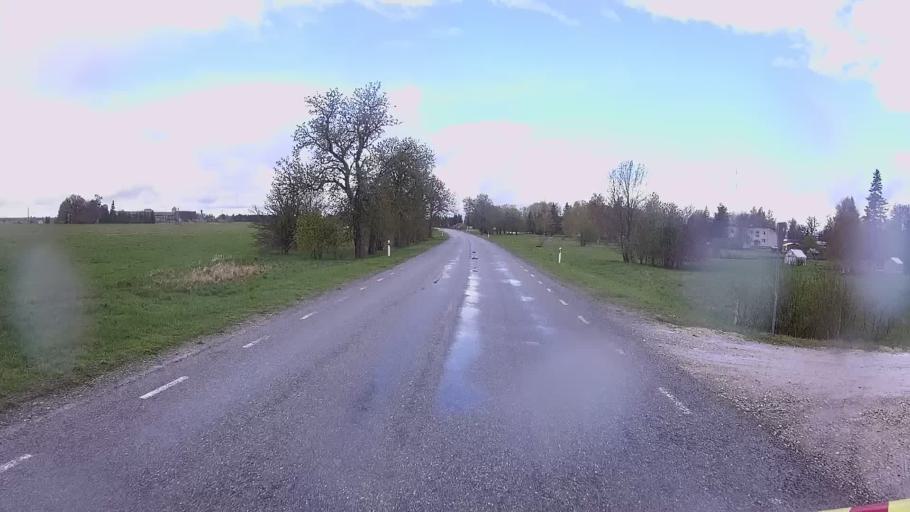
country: EE
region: Hiiumaa
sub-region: Kaerdla linn
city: Kardla
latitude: 58.8349
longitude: 22.8030
